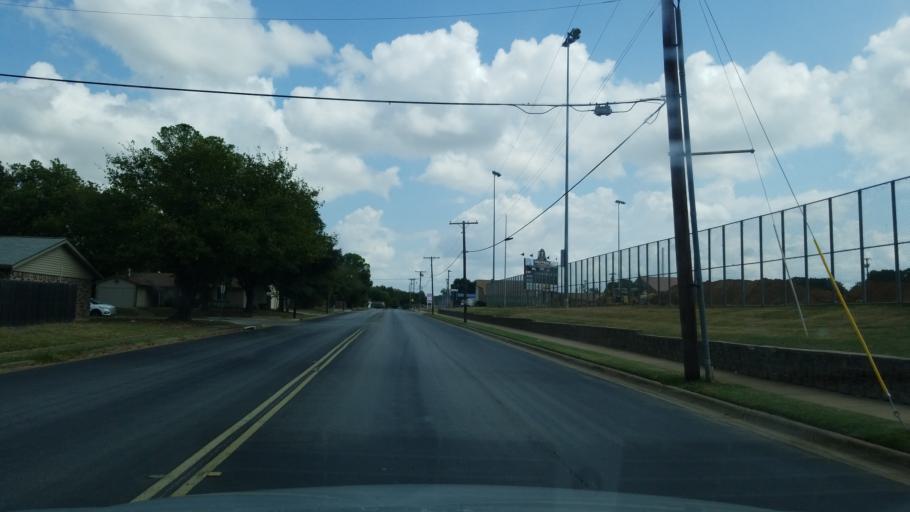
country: US
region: Texas
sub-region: Tarrant County
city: Euless
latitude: 32.8449
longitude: -97.0967
